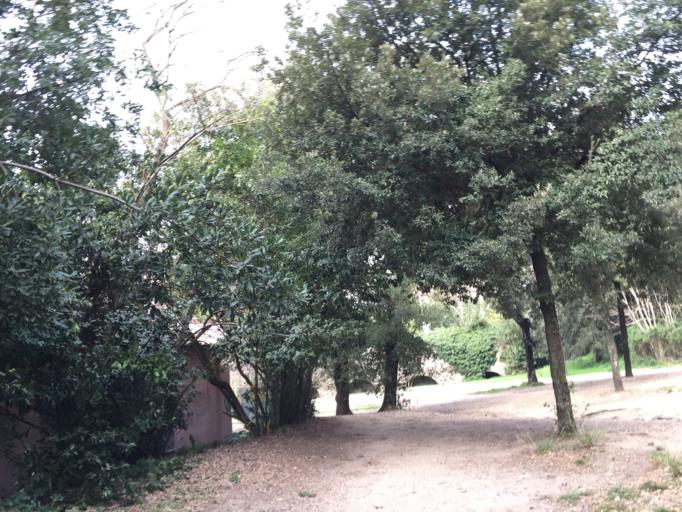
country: VA
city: Vatican City
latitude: 41.8881
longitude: 12.4541
